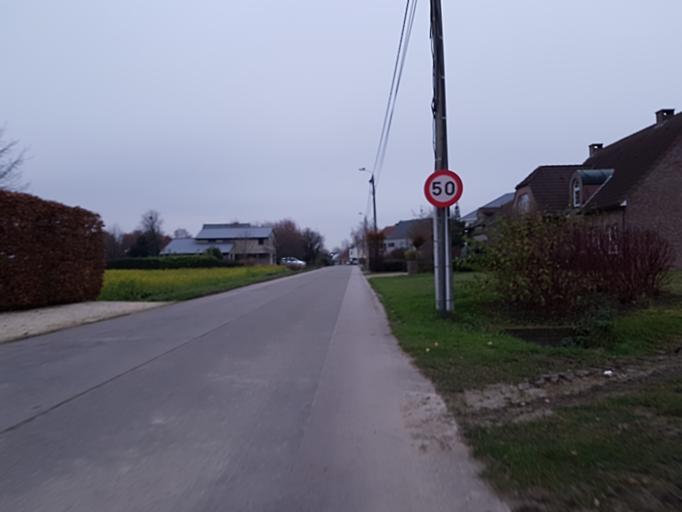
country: BE
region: Flanders
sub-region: Provincie Vlaams-Brabant
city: Zemst
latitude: 51.0180
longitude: 4.4208
